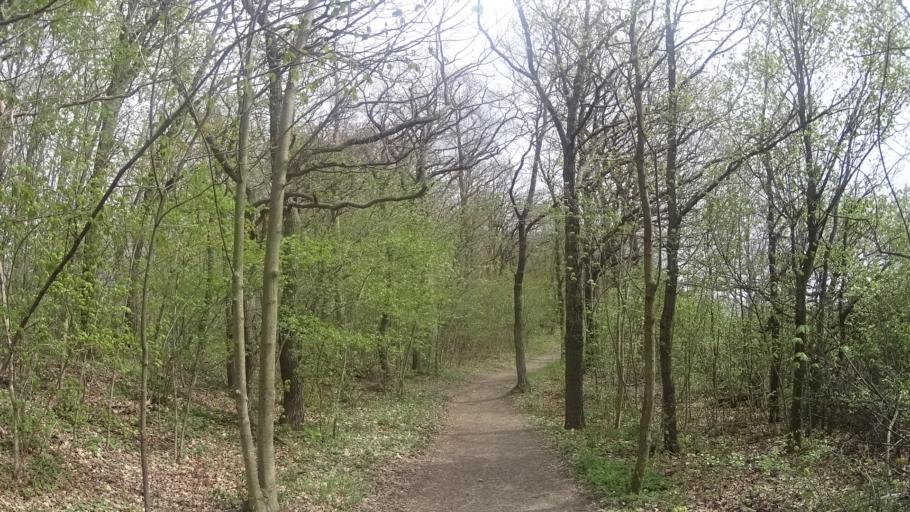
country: DE
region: Thuringia
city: Wandersleben
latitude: 50.8611
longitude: 10.8492
